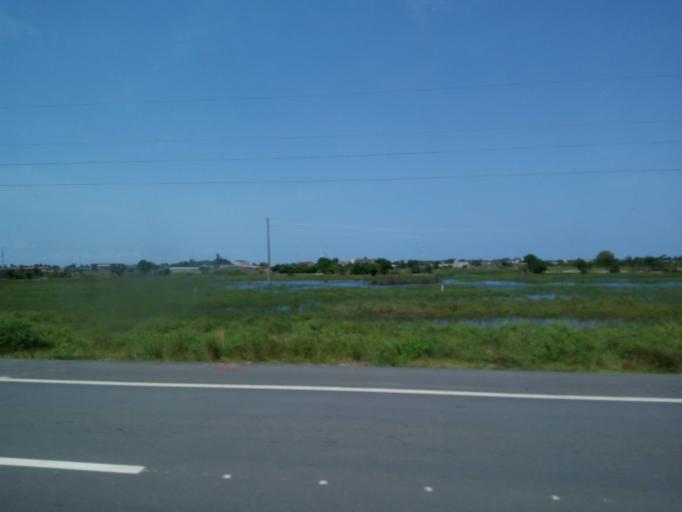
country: CI
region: Sud-Comoe
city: Grand-Bassam
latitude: 5.2272
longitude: -3.7420
